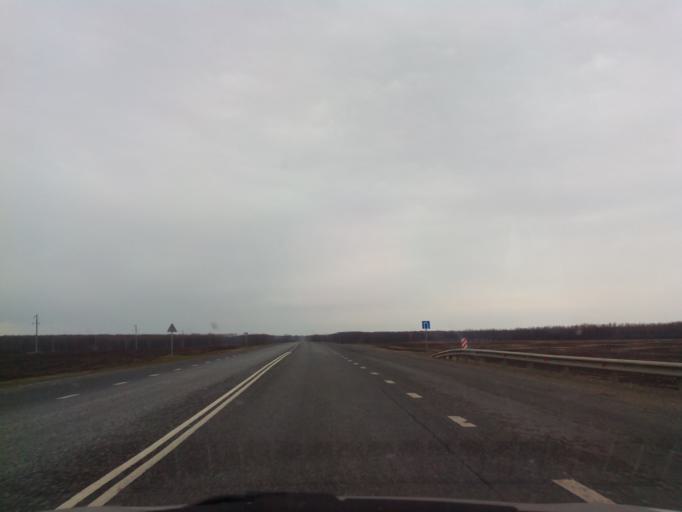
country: RU
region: Tambov
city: Zavoronezhskoye
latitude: 52.9898
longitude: 40.5566
